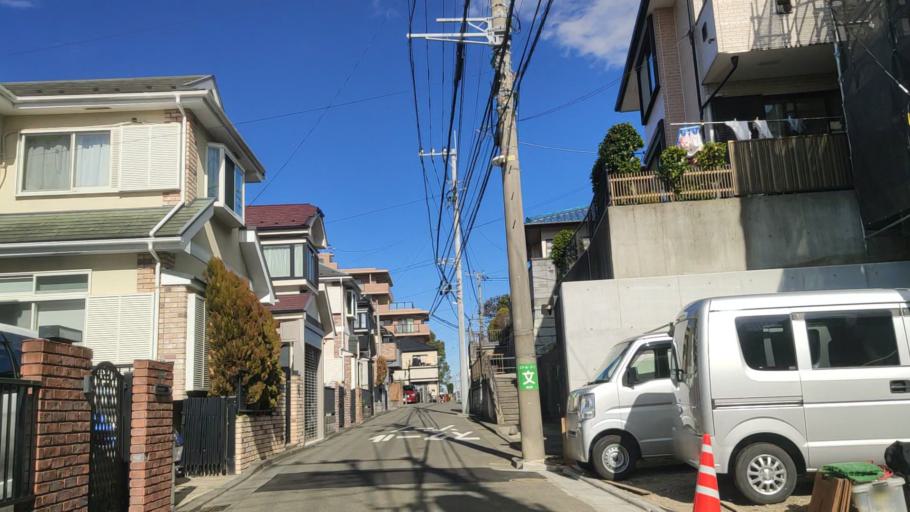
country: JP
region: Kanagawa
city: Yokohama
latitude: 35.4772
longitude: 139.5787
